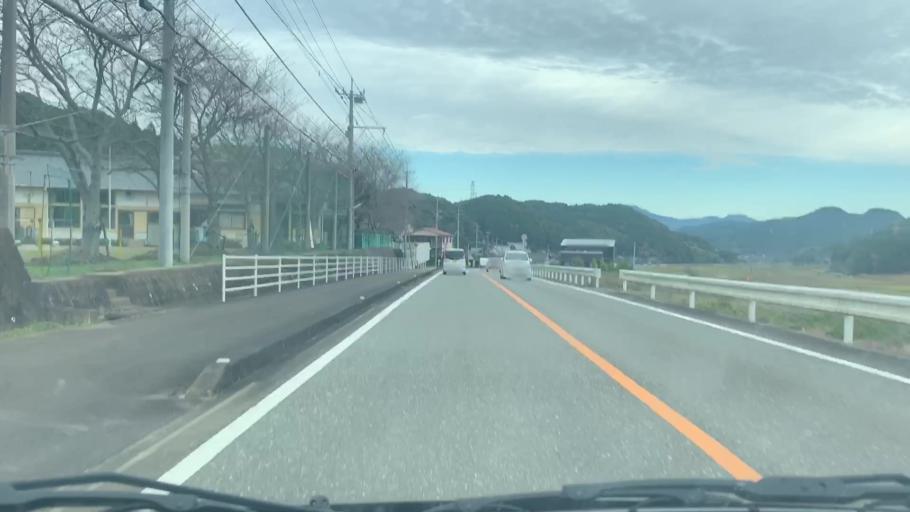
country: JP
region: Saga Prefecture
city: Takeocho-takeo
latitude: 33.1730
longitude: 129.9697
